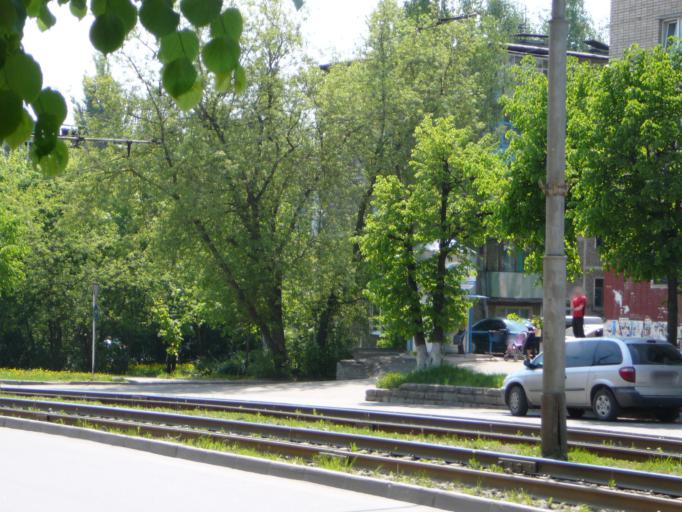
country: RU
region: Smolensk
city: Smolensk
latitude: 54.7760
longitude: 32.0243
